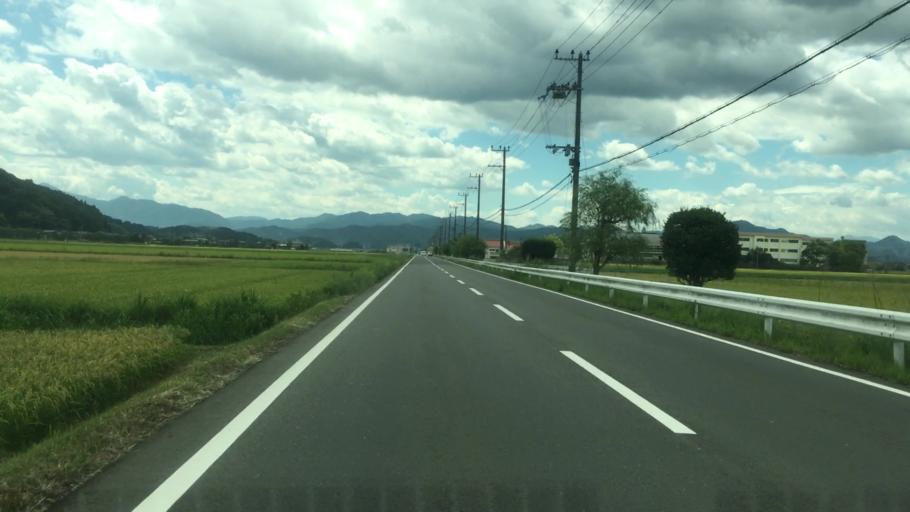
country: JP
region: Hyogo
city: Toyooka
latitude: 35.5336
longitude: 134.8397
